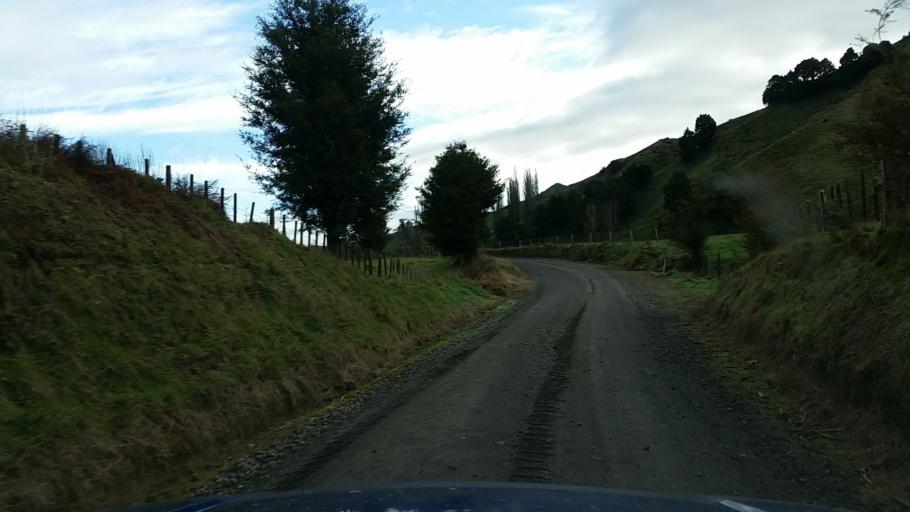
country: NZ
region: Taranaki
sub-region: New Plymouth District
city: Waitara
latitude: -39.0903
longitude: 174.8360
